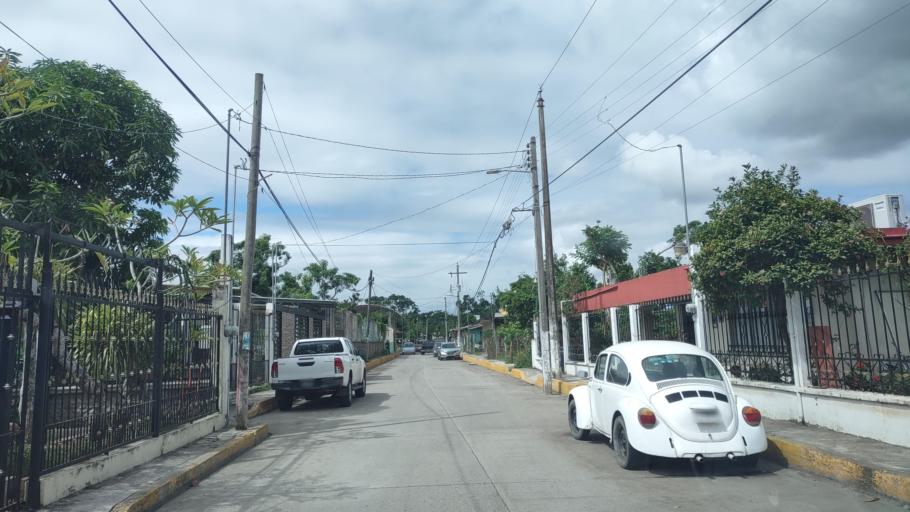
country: MX
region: Veracruz
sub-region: Papantla
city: Residencial Tajin
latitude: 20.5957
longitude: -97.4209
